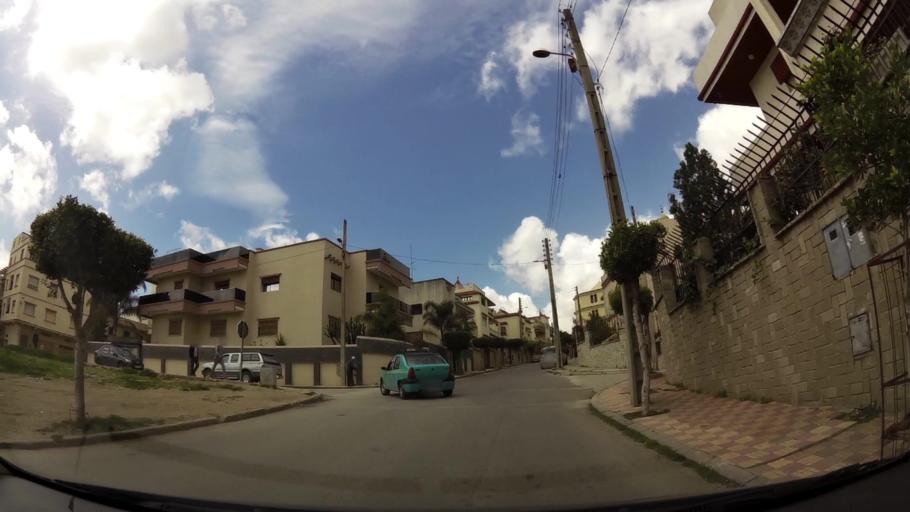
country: MA
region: Tanger-Tetouan
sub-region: Tanger-Assilah
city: Tangier
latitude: 35.7616
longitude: -5.8130
